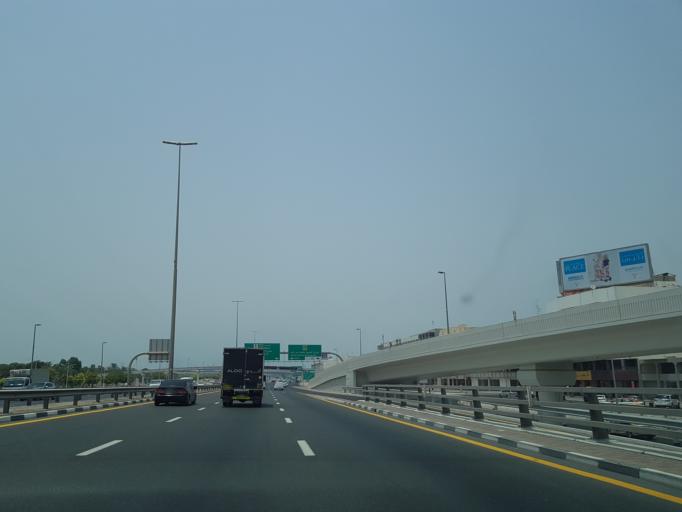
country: AE
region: Ash Shariqah
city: Sharjah
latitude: 25.2359
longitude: 55.3027
